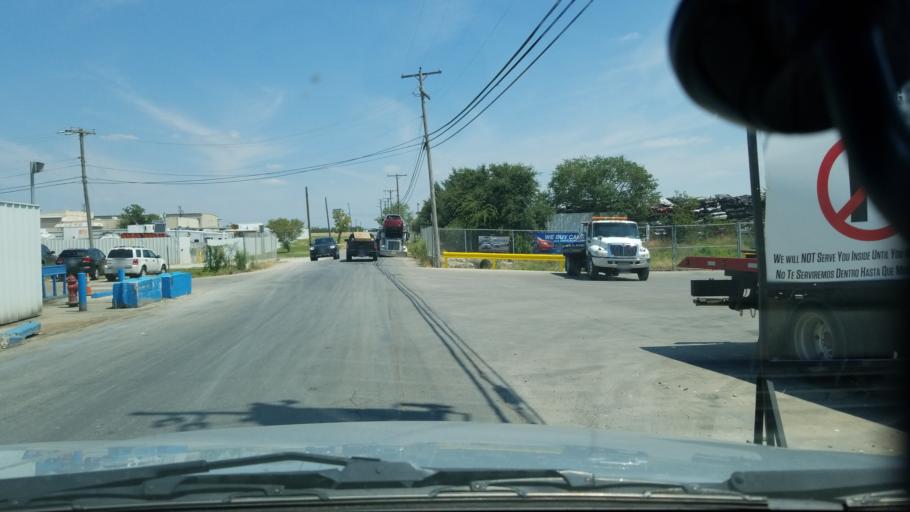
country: US
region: Texas
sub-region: Dallas County
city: Grand Prairie
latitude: 32.7426
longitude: -96.9533
